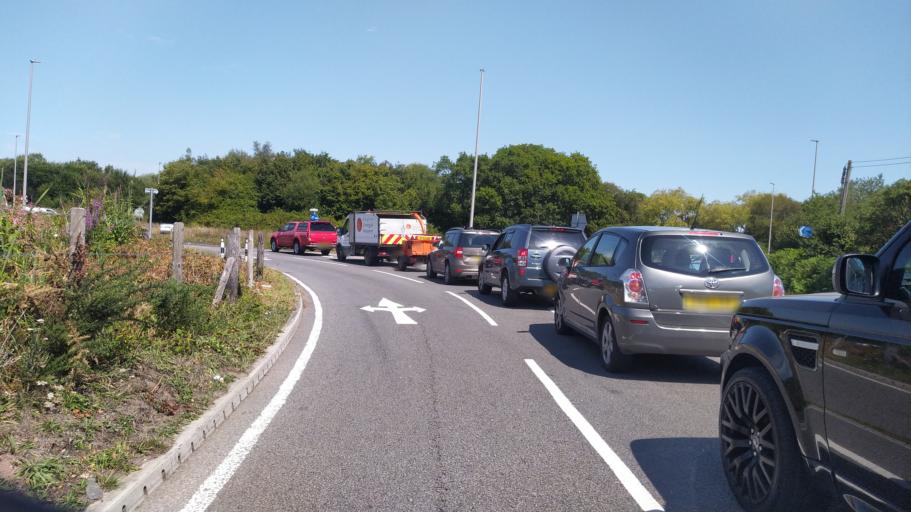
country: GB
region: England
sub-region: Dorset
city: Lytchett Matravers
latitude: 50.7318
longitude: -2.0658
